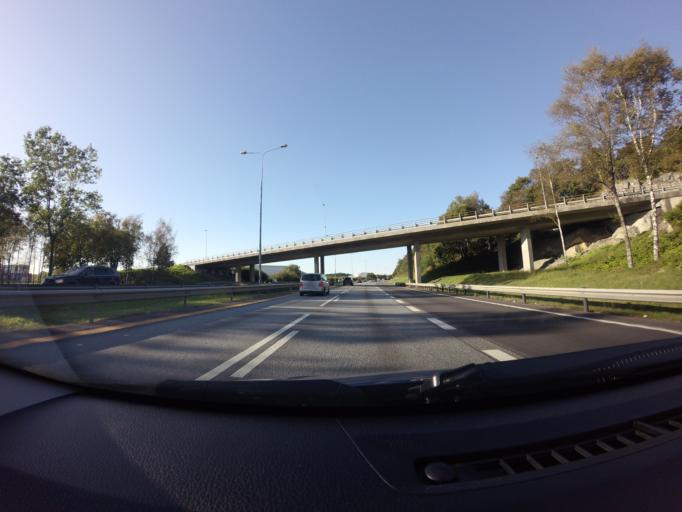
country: NO
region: Rogaland
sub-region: Sandnes
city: Sandnes
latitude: 58.8942
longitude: 5.7122
